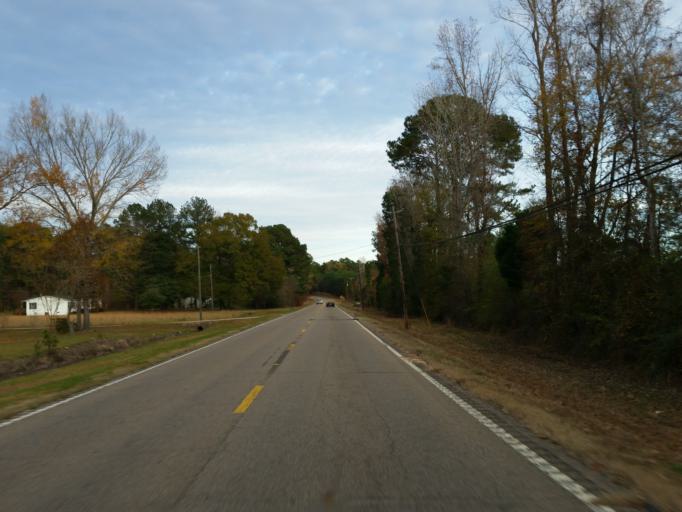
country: US
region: Mississippi
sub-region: Lauderdale County
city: Marion
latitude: 32.4123
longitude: -88.5487
